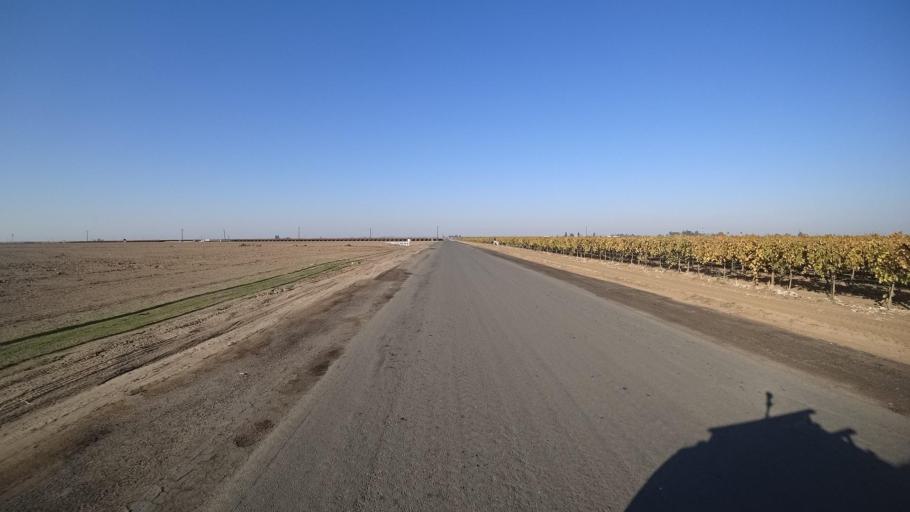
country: US
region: California
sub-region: Tulare County
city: Richgrove
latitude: 35.7687
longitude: -119.1665
